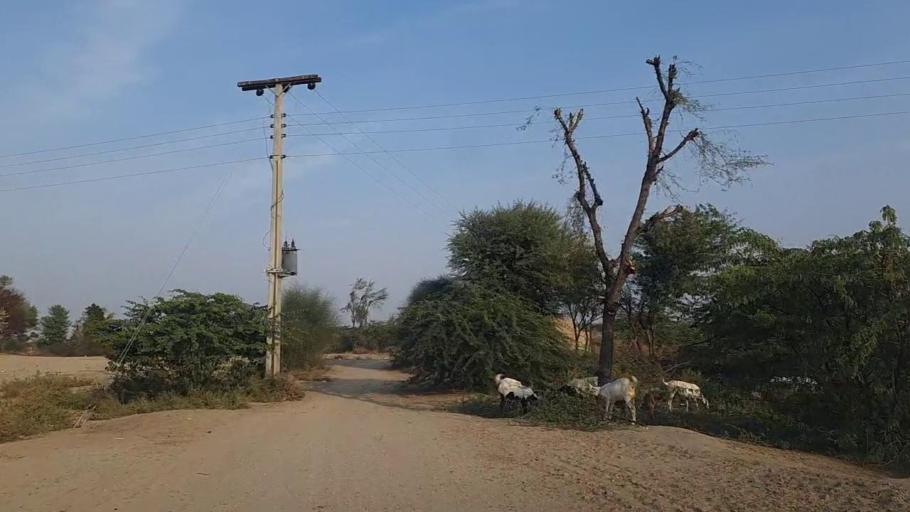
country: PK
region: Sindh
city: Jam Sahib
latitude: 26.4370
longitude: 68.6007
